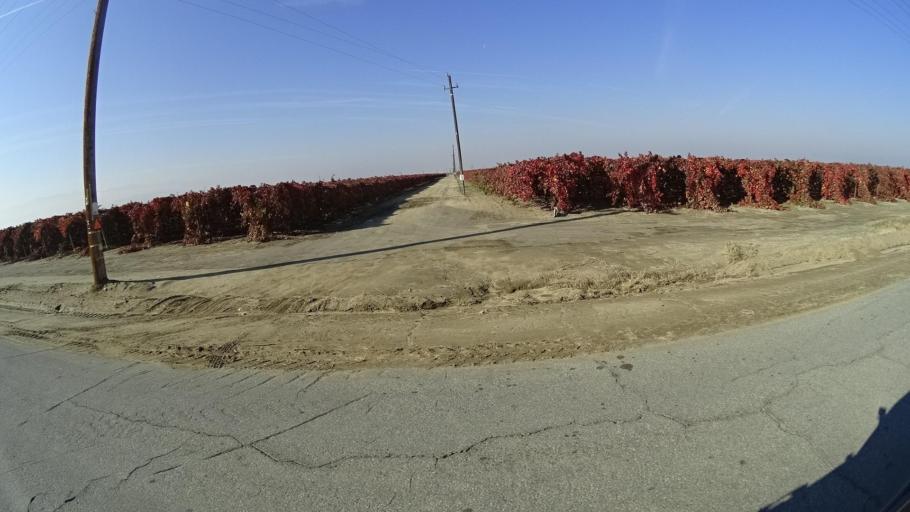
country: US
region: California
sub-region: Kern County
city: Arvin
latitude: 35.1000
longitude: -118.8778
